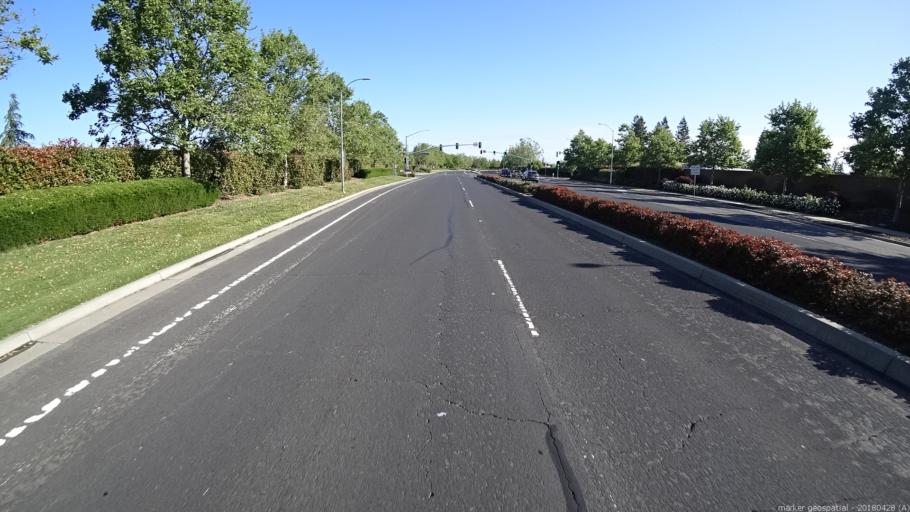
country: US
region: California
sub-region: Yolo County
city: West Sacramento
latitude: 38.5503
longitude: -121.5669
